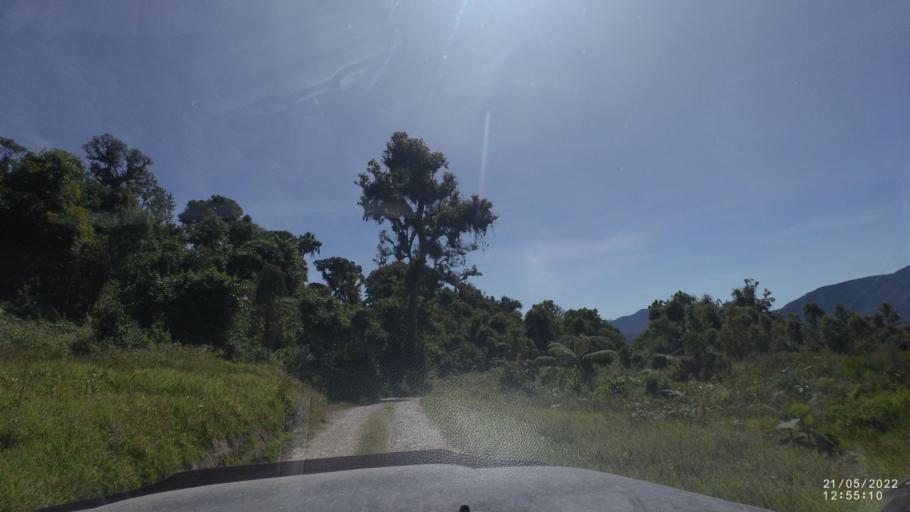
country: BO
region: Cochabamba
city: Colomi
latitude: -17.1763
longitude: -65.9432
